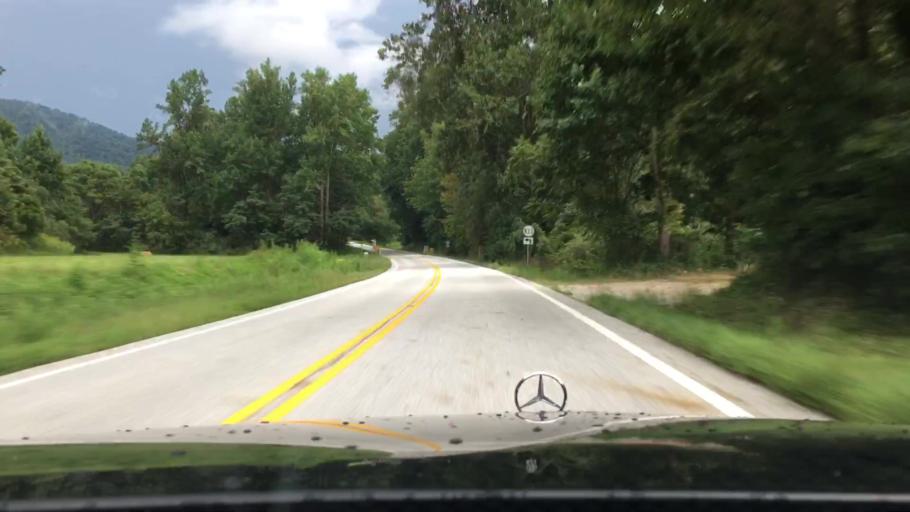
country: US
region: Virginia
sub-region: Nelson County
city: Nellysford
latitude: 37.8285
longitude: -78.9348
